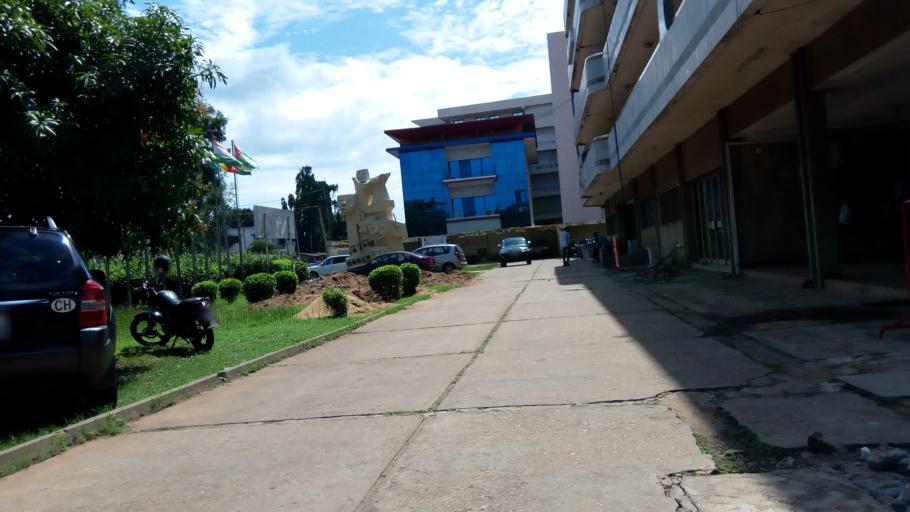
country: TG
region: Maritime
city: Lome
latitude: 6.1255
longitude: 1.2107
